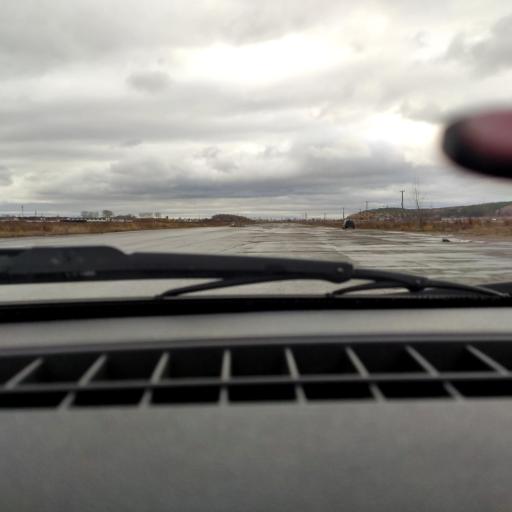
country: RU
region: Bashkortostan
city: Ufa
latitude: 54.8319
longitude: 56.1680
